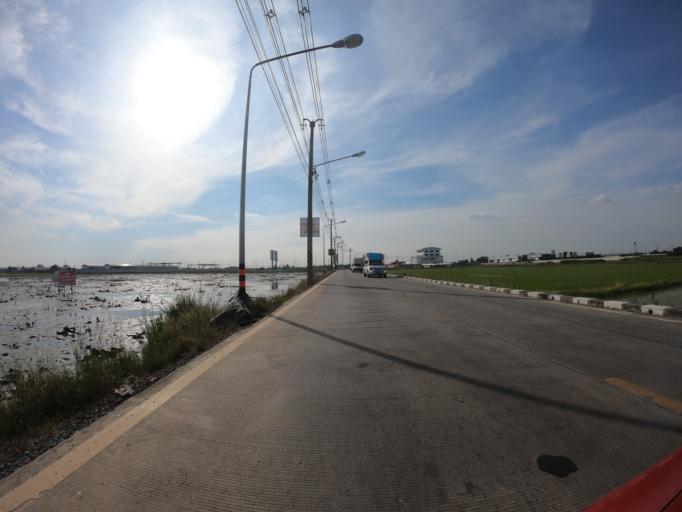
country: TH
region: Pathum Thani
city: Lam Luk Ka
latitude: 13.9613
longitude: 100.7184
